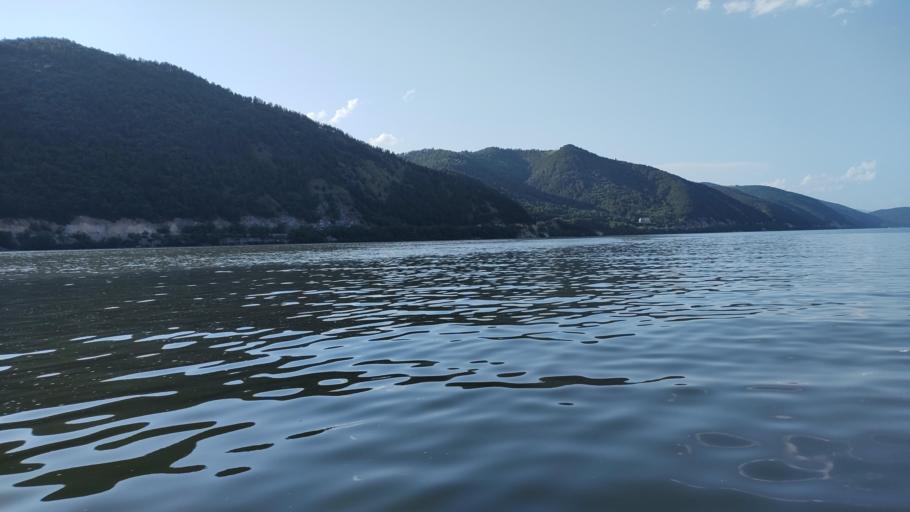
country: RO
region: Mehedinti
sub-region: Comuna Svinita
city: Svinita
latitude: 44.5066
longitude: 22.1957
